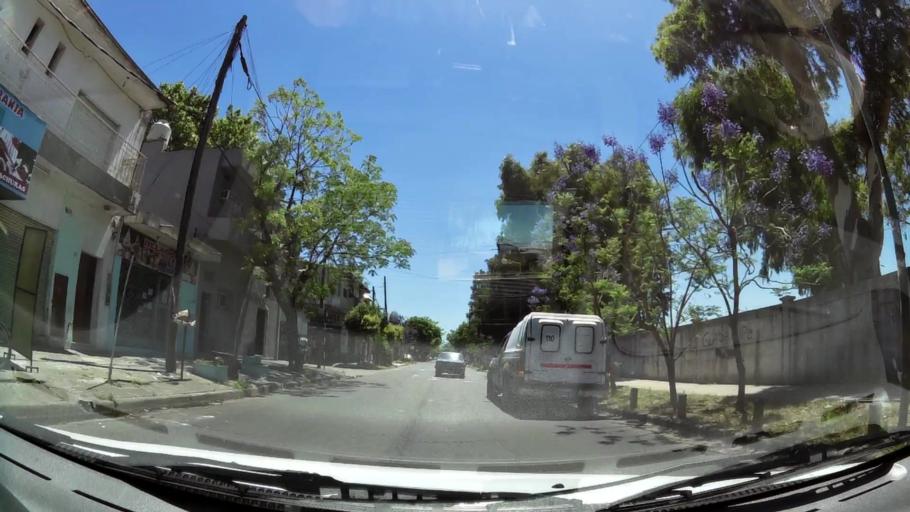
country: AR
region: Buenos Aires
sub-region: Partido de General San Martin
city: General San Martin
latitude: -34.5485
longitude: -58.5288
